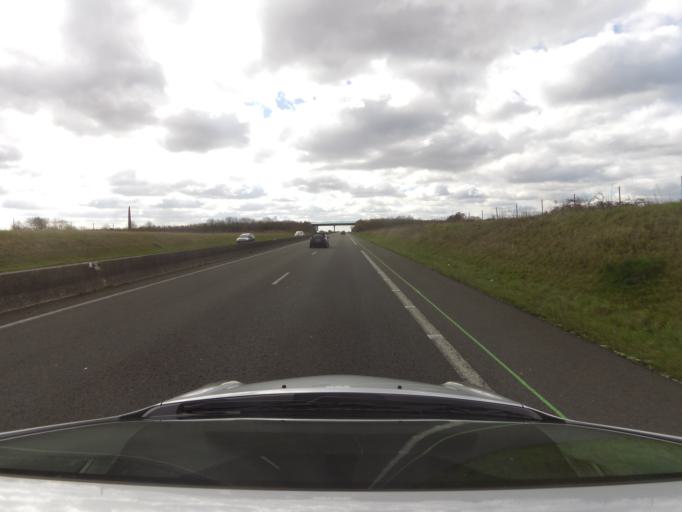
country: FR
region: Picardie
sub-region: Departement de la Somme
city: Nouvion
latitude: 50.2303
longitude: 1.7519
